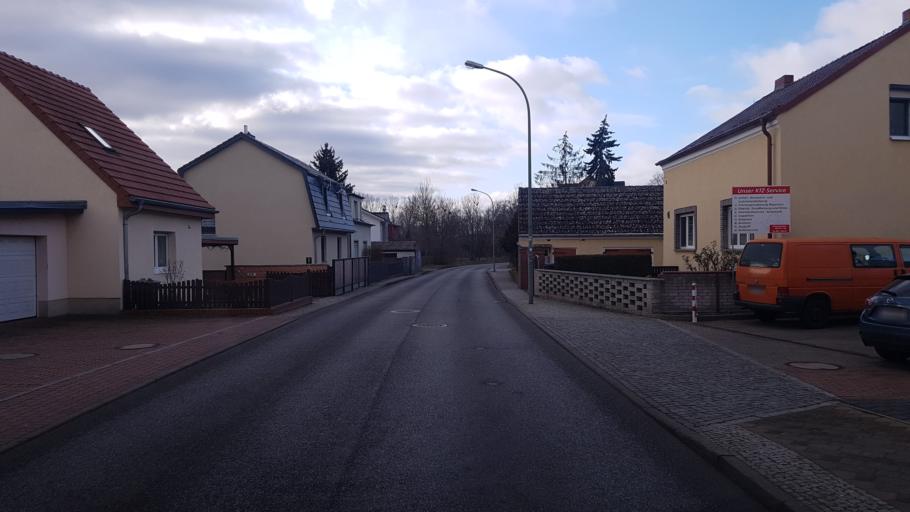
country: DE
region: Berlin
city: Wannsee
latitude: 52.3613
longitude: 13.1236
